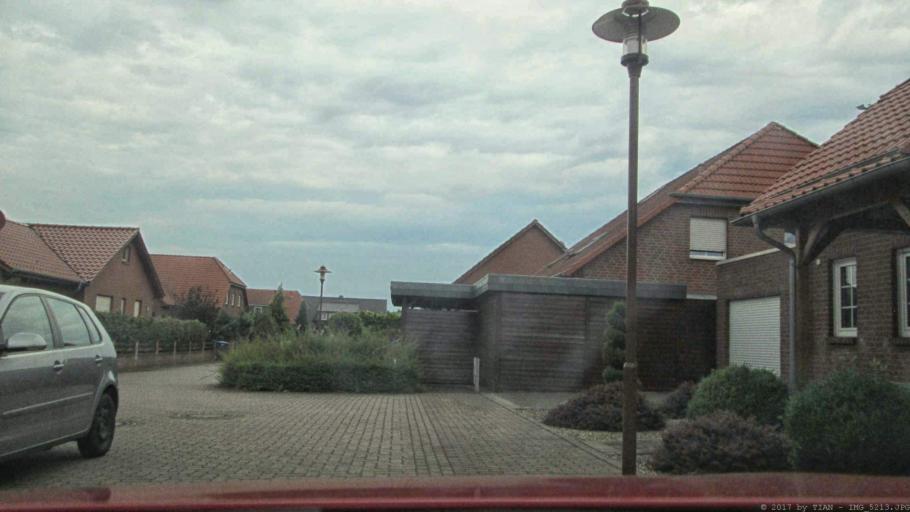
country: DE
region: Lower Saxony
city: Wolfsburg
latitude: 52.4106
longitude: 10.8458
